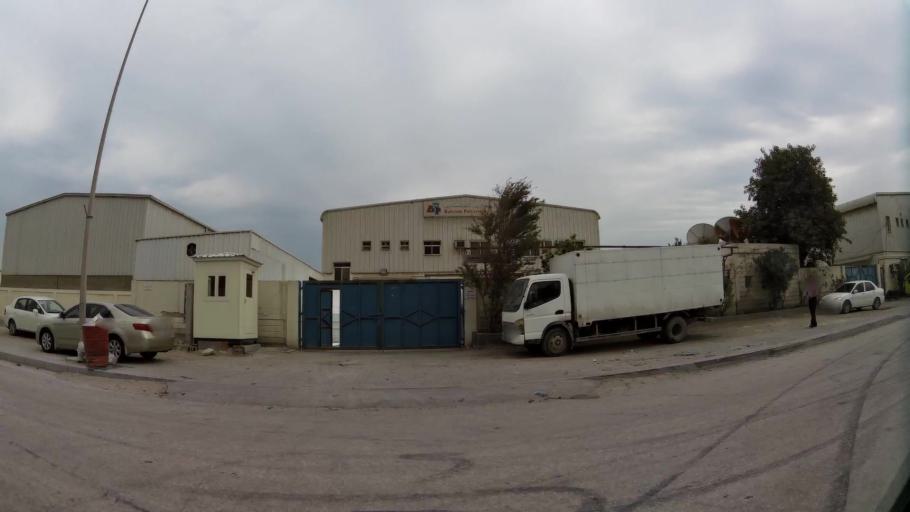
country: BH
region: Northern
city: Sitrah
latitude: 26.1811
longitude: 50.6155
